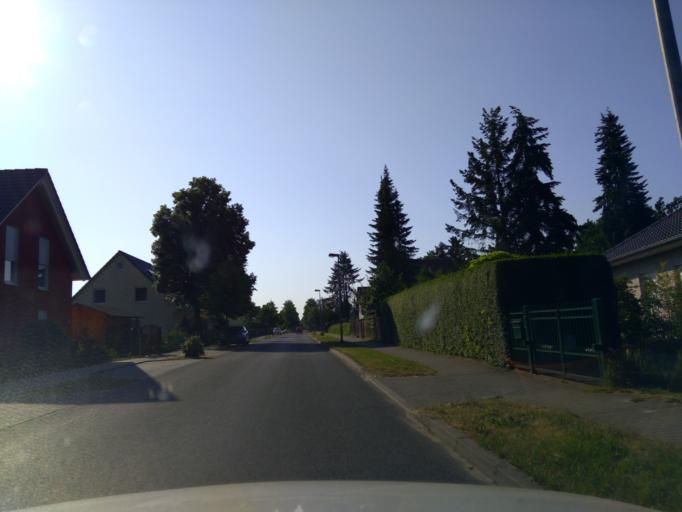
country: DE
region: Brandenburg
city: Dallgow-Doeberitz
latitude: 52.5600
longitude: 13.0681
